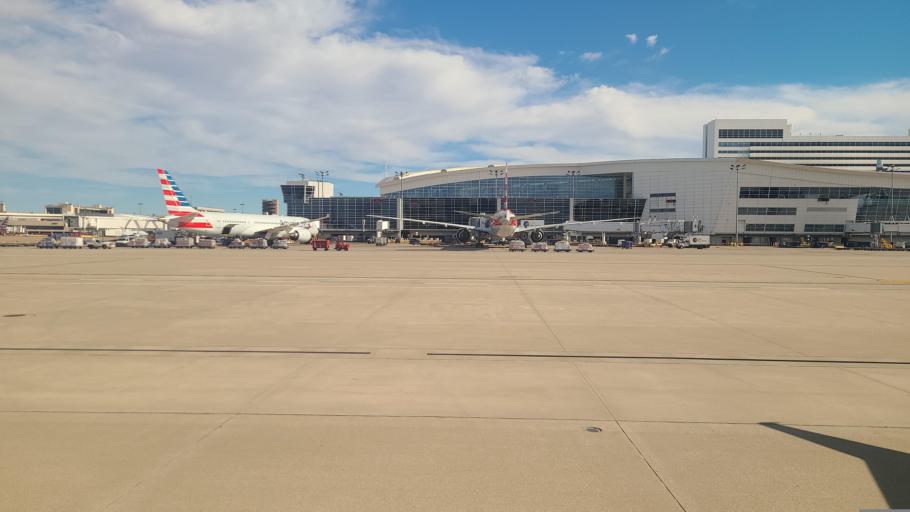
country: US
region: Texas
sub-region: Tarrant County
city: Grapevine
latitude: 32.8989
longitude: -97.0477
